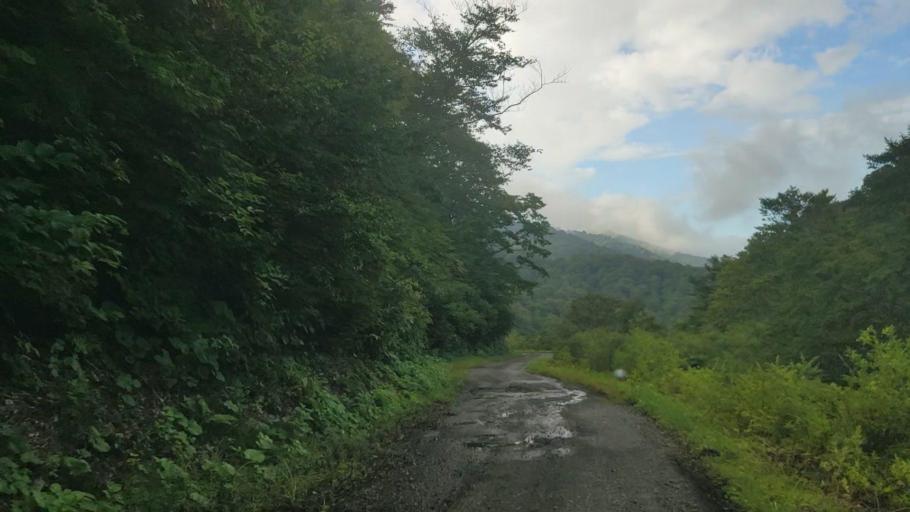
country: JP
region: Toyama
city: Yatsuomachi-higashikumisaka
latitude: 36.3525
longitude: 137.0642
